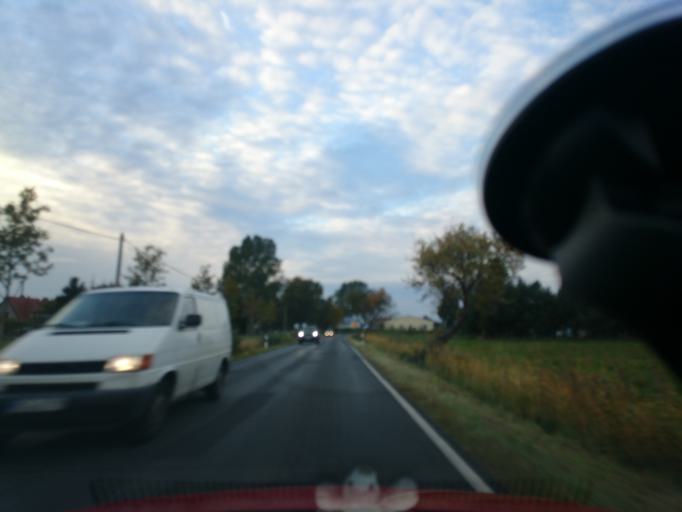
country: DE
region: Mecklenburg-Vorpommern
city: Zingst
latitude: 54.3713
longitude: 12.6278
